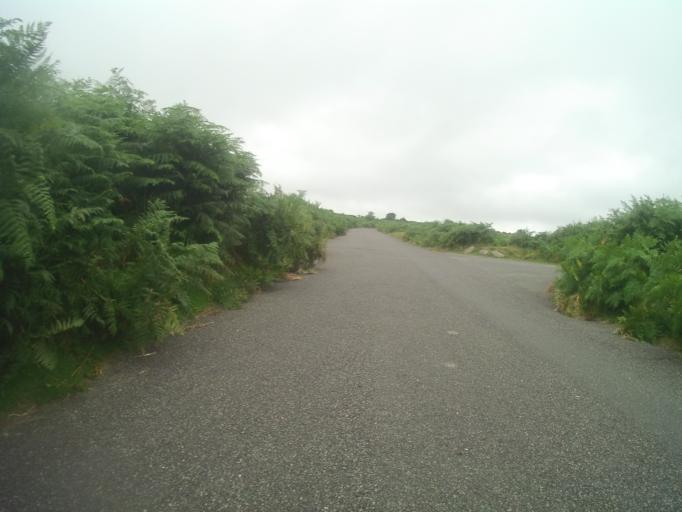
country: GB
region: England
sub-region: Devon
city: Buckfastleigh
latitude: 50.5259
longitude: -3.8563
